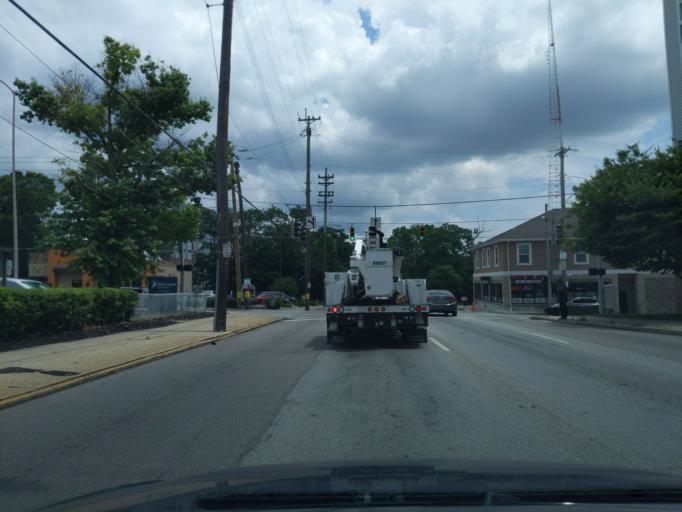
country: US
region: Kentucky
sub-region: Campbell County
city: Bellevue
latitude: 39.1268
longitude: -84.5039
